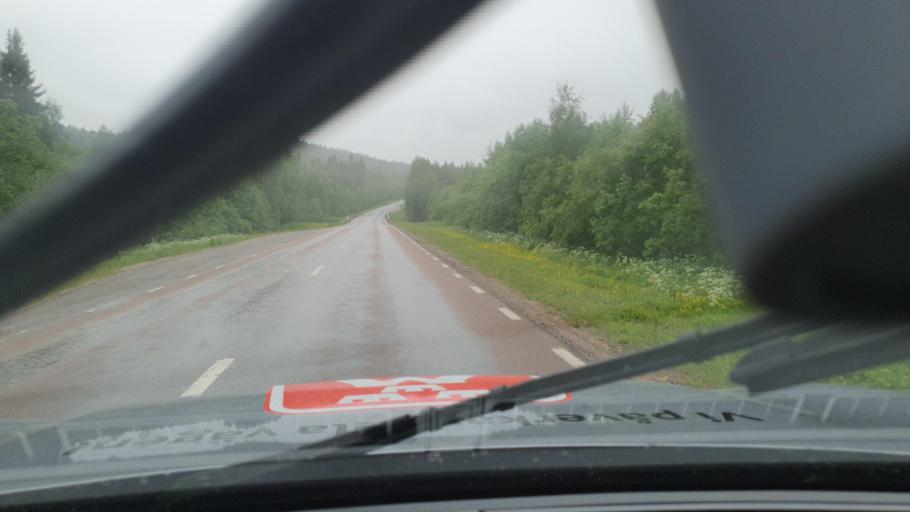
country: SE
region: Norrbotten
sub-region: Overtornea Kommun
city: OEvertornea
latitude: 66.4384
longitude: 23.3255
